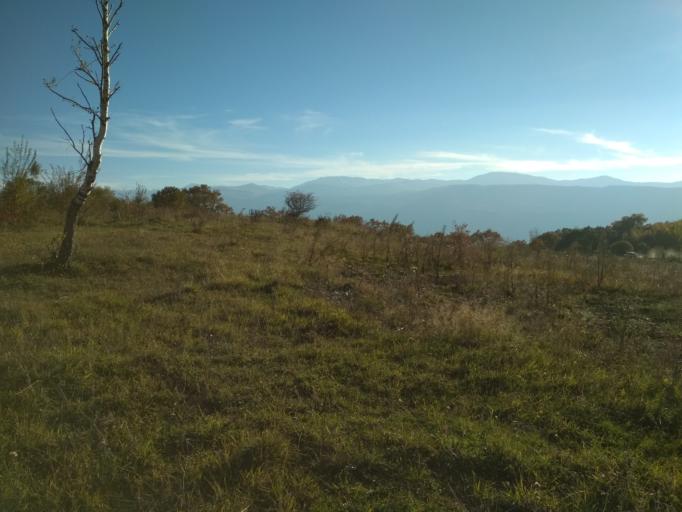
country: RU
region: Adygeya
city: Kamennomostskiy
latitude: 44.2229
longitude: 39.9959
